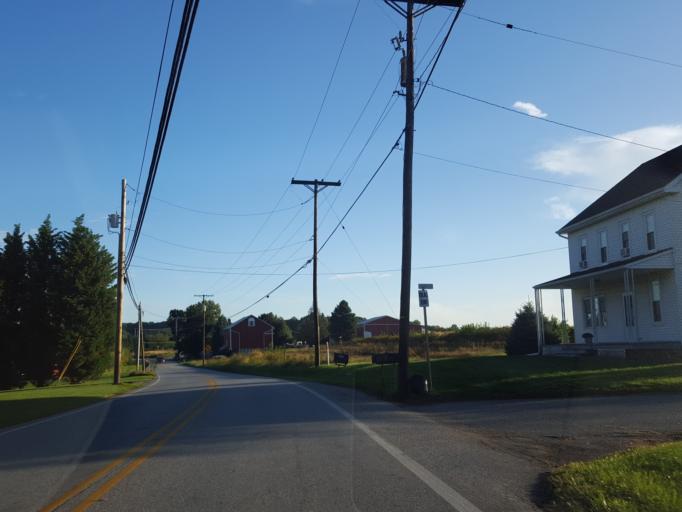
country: US
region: Pennsylvania
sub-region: York County
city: Red Lion
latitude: 39.9120
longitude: -76.6081
